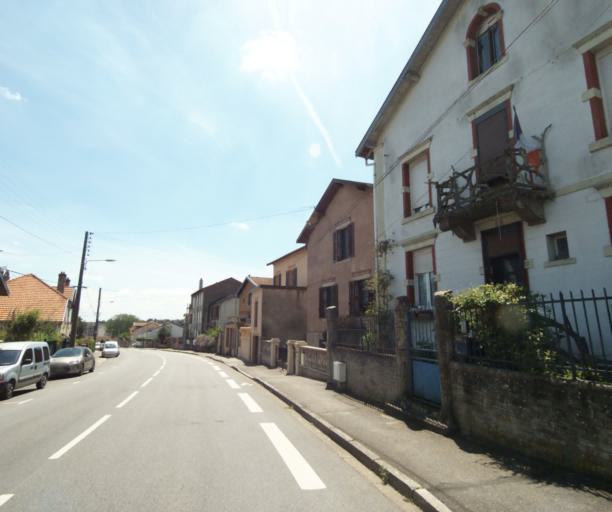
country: FR
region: Lorraine
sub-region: Departement de Meurthe-et-Moselle
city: Luneville
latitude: 48.6036
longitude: 6.4879
